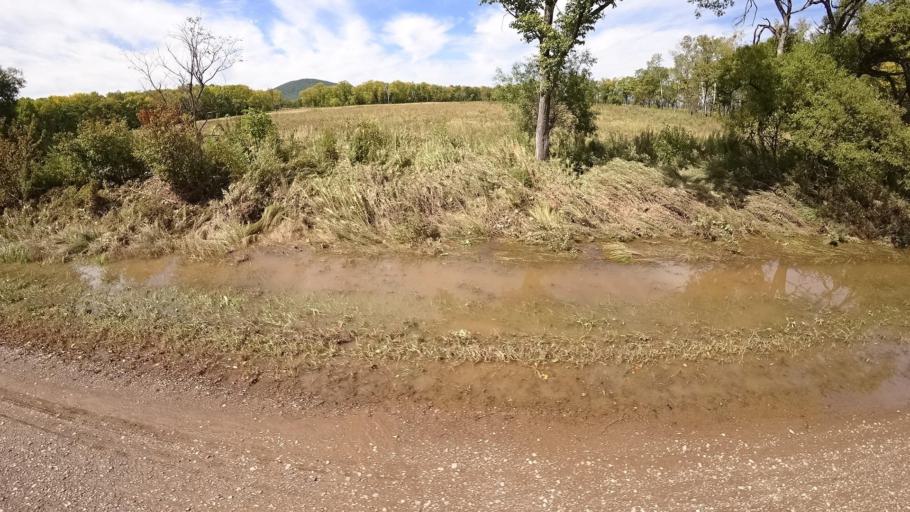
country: RU
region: Primorskiy
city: Yakovlevka
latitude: 44.6626
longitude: 133.7503
